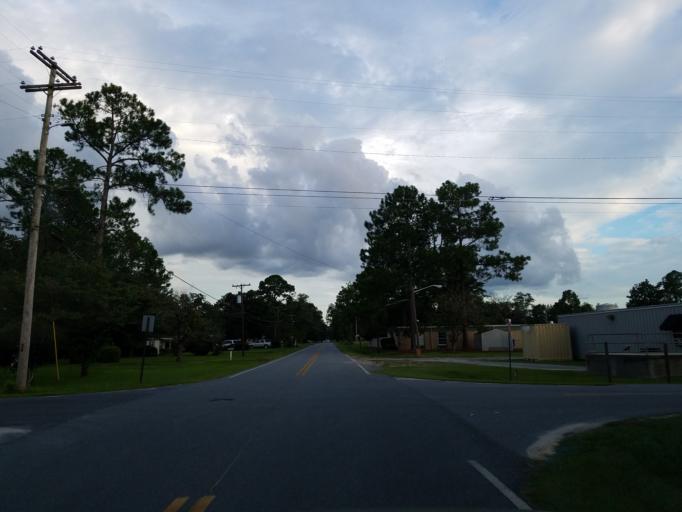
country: US
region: Georgia
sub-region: Cook County
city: Adel
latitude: 31.1456
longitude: -83.4238
